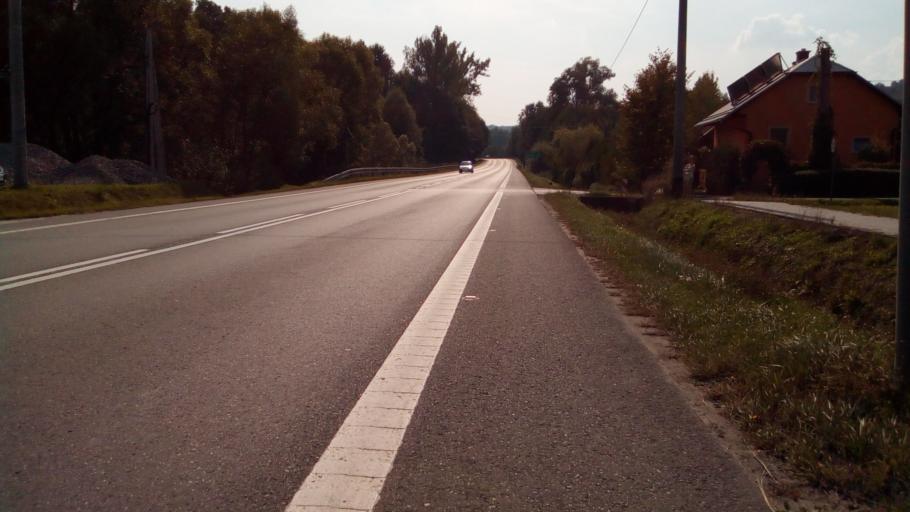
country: PL
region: Subcarpathian Voivodeship
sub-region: Powiat strzyzowski
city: Niebylec
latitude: 49.8534
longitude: 21.9000
